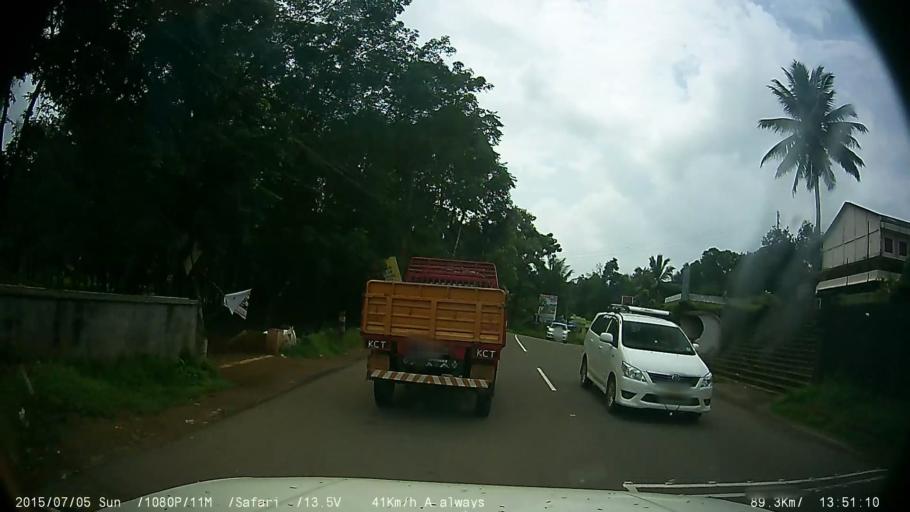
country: IN
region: Kerala
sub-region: Kottayam
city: Palackattumala
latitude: 9.7432
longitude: 76.6108
